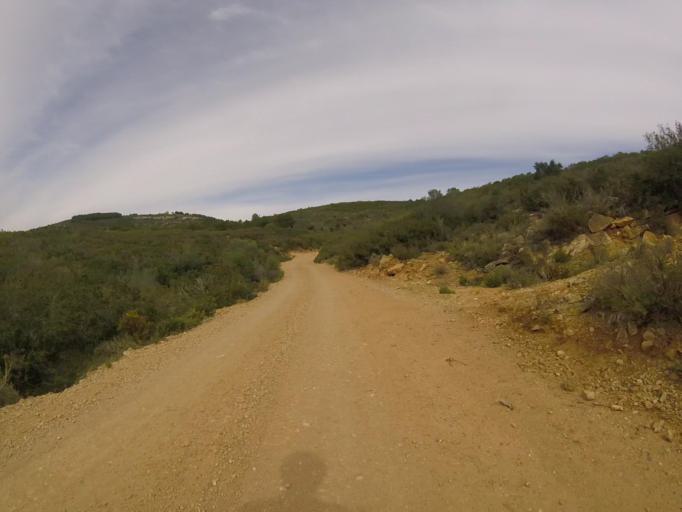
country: ES
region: Valencia
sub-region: Provincia de Castello
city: Cabanes
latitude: 40.1903
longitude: 0.0907
